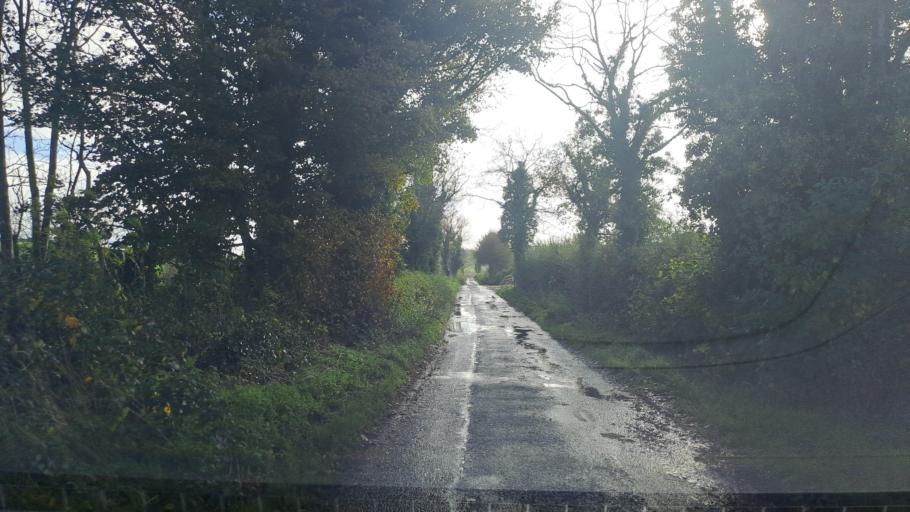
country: IE
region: Ulster
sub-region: An Cabhan
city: Cootehill
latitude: 53.9981
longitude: -7.0278
